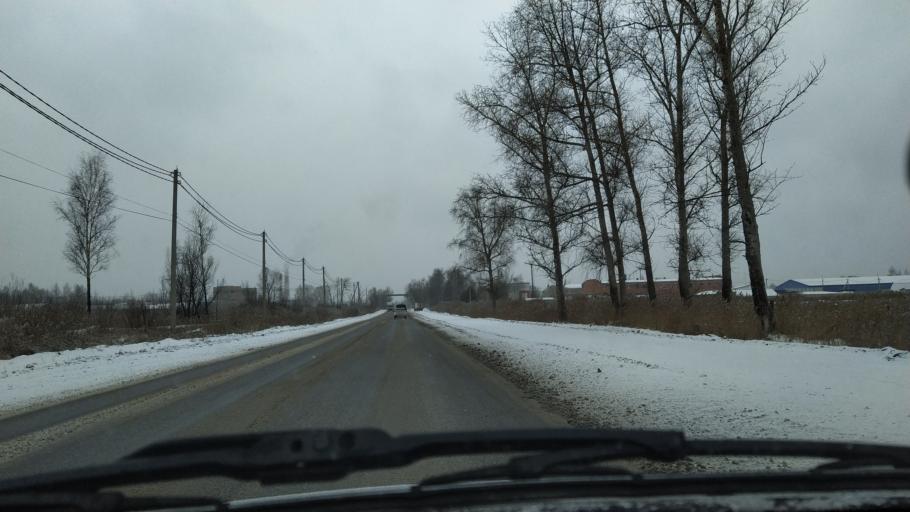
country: RU
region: Moskovskaya
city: Lopatinskiy
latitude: 55.3502
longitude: 38.7397
